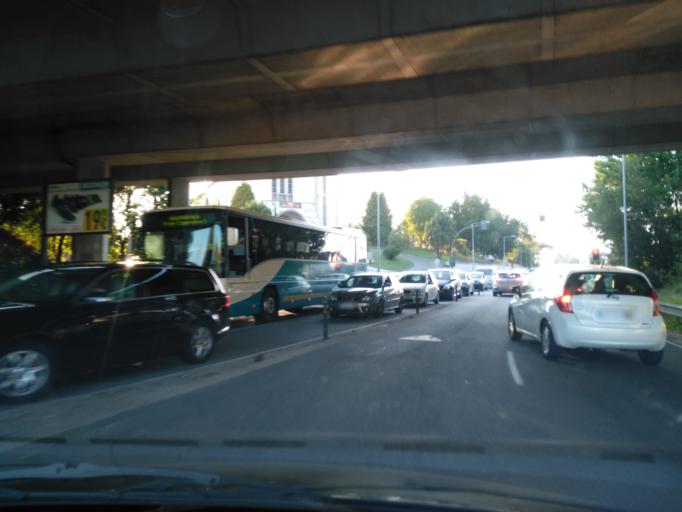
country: PT
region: Braga
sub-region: Guimaraes
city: Candoso
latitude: 41.4441
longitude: -8.3356
